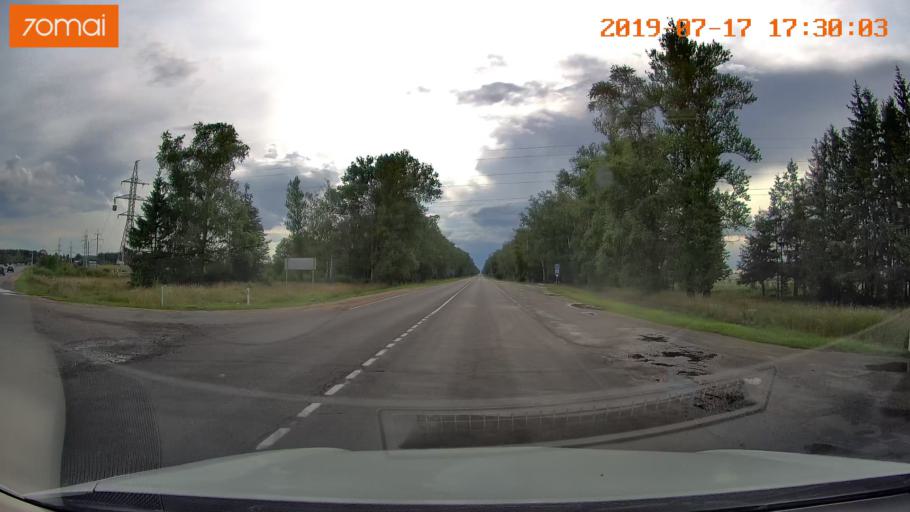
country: BY
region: Mogilev
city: Babruysk
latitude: 53.1208
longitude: 29.1517
